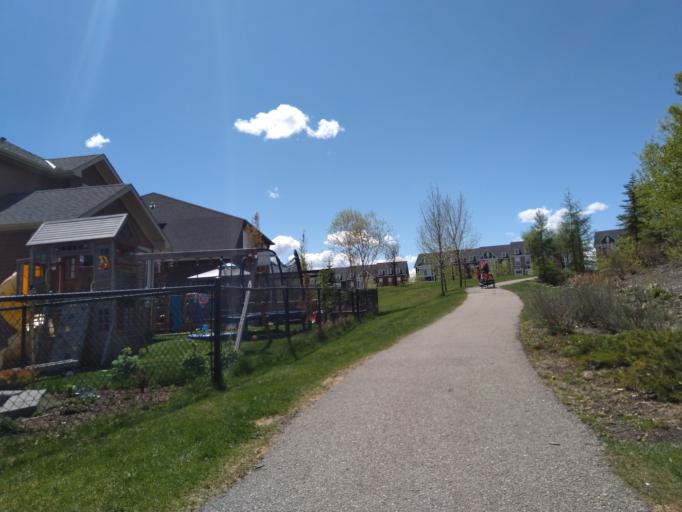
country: CA
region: Alberta
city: Chestermere
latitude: 51.0259
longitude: -113.8363
